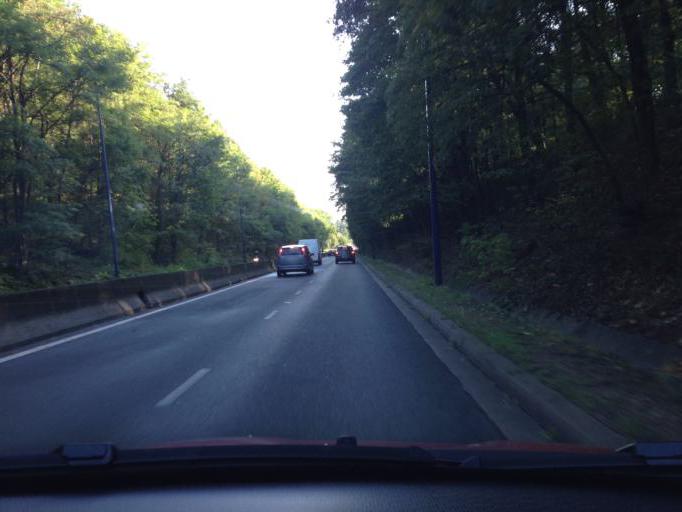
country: FR
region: Ile-de-France
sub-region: Departement des Hauts-de-Seine
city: Clamart
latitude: 48.7998
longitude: 2.2541
